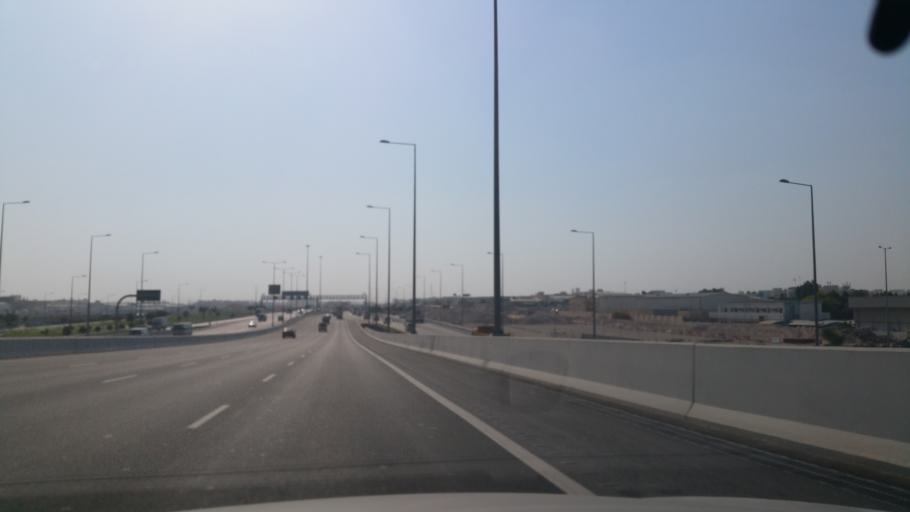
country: QA
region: Al Wakrah
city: Al Wukayr
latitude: 25.1915
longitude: 51.4526
